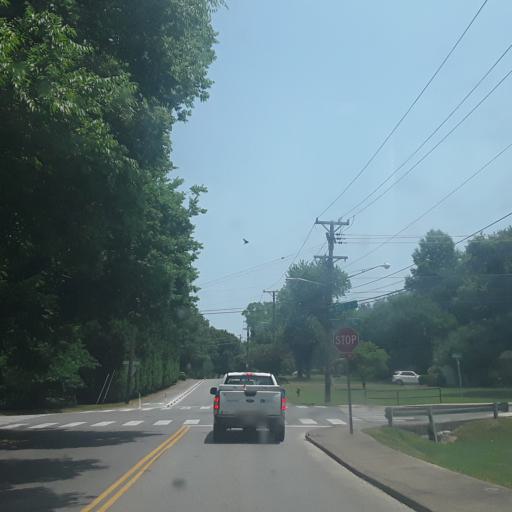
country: US
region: Tennessee
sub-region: Williamson County
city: Brentwood
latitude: 36.0477
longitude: -86.7530
